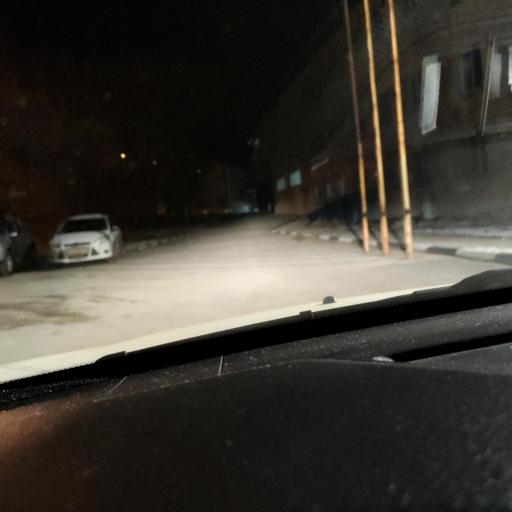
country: RU
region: Samara
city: Smyshlyayevka
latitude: 53.2375
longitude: 50.4809
